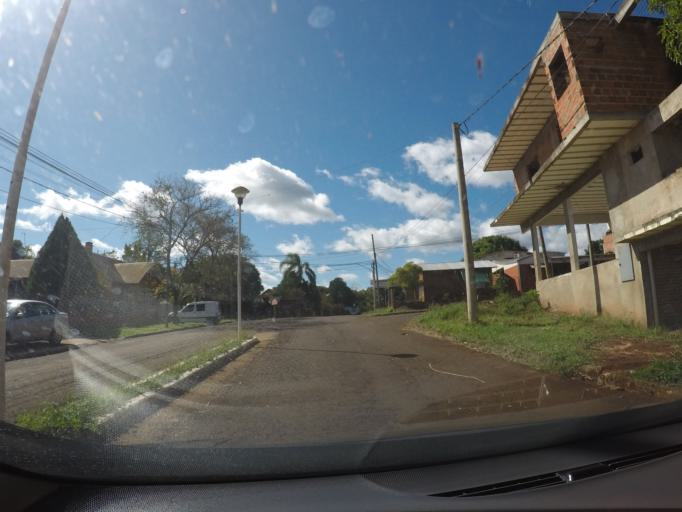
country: AR
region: Misiones
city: Puerto Rico
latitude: -26.7980
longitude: -55.0187
